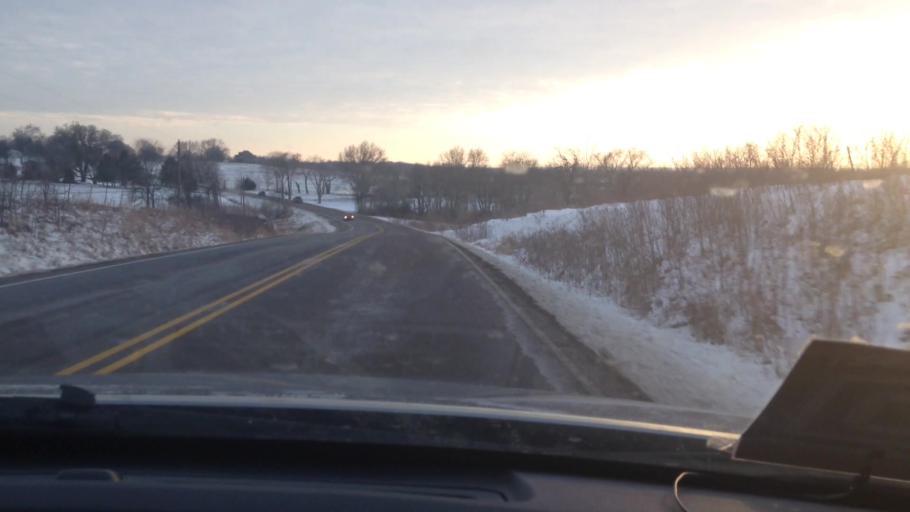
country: US
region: Kansas
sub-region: Leavenworth County
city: Lansing
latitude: 39.2553
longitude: -94.9738
